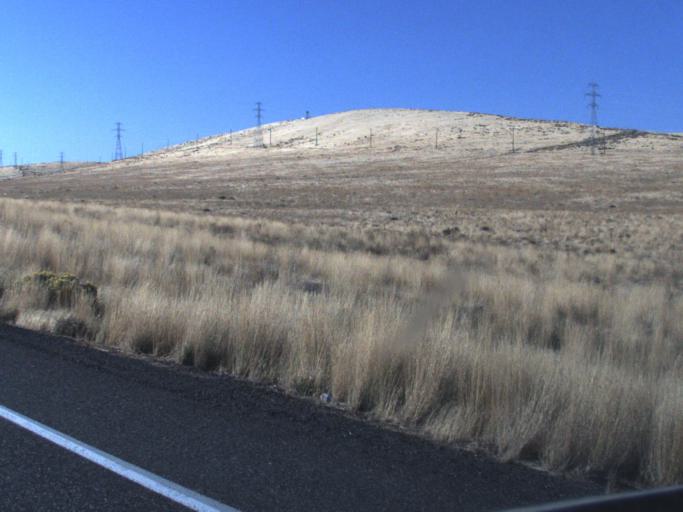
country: US
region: Washington
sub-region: Benton County
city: Highland
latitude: 46.1535
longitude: -119.1449
